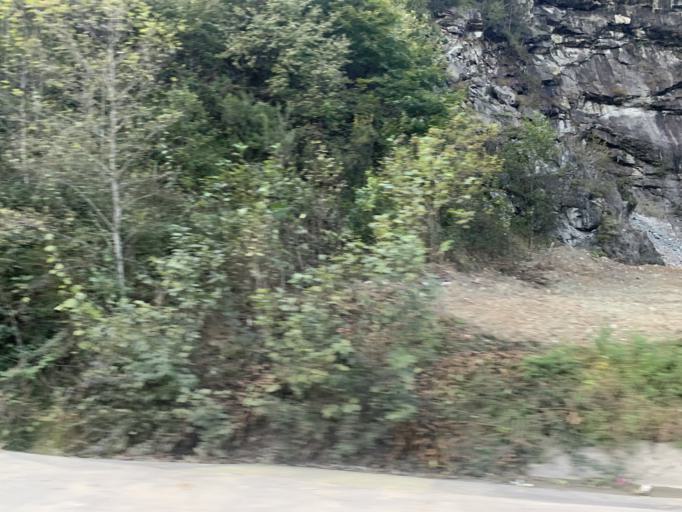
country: TR
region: Trabzon
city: Of
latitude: 40.8767
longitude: 40.2805
